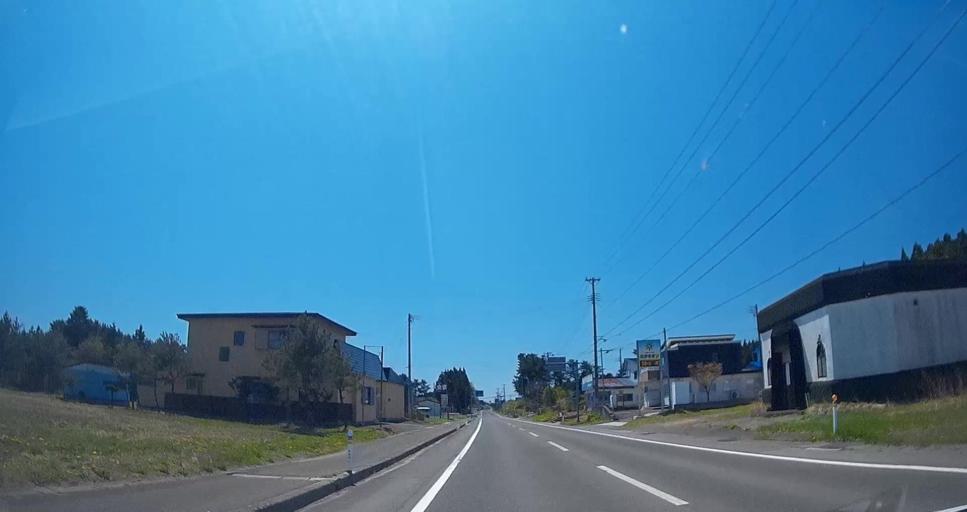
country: JP
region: Aomori
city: Mutsu
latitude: 41.0813
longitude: 141.3858
